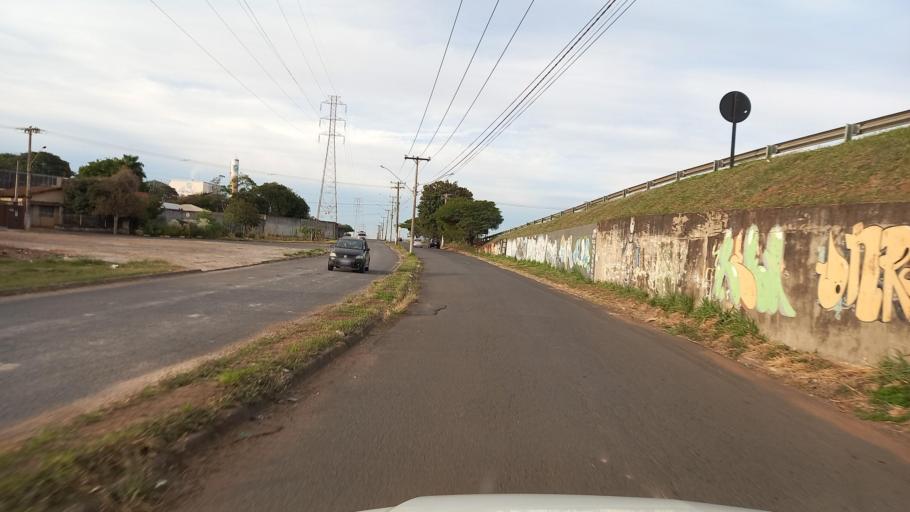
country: BR
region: Sao Paulo
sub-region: Moji-Guacu
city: Mogi-Gaucu
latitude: -22.3425
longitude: -46.9468
